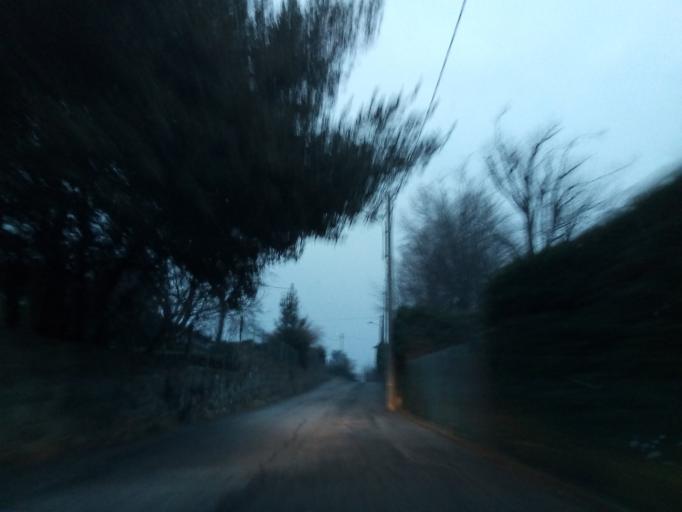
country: IT
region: Piedmont
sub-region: Provincia di Torino
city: Ivrea
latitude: 45.4804
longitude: 7.8776
